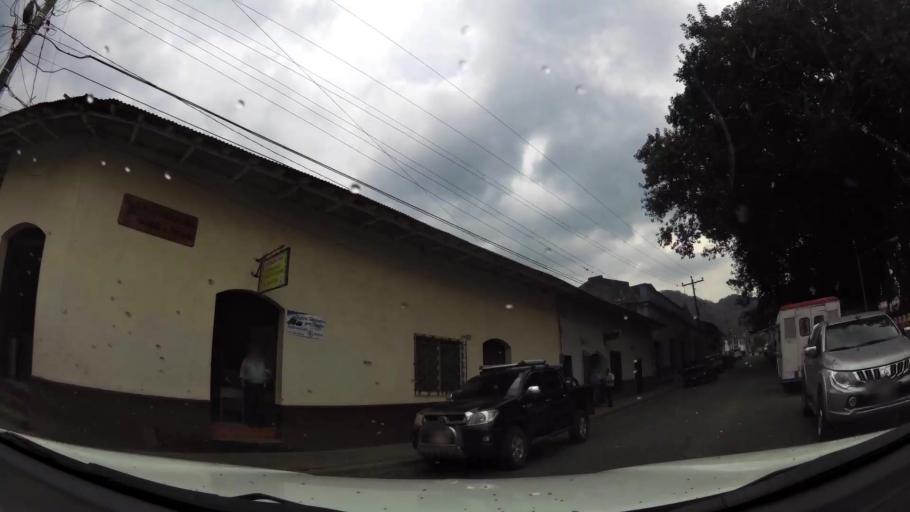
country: NI
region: Jinotega
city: Jinotega
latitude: 13.0926
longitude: -86.0035
